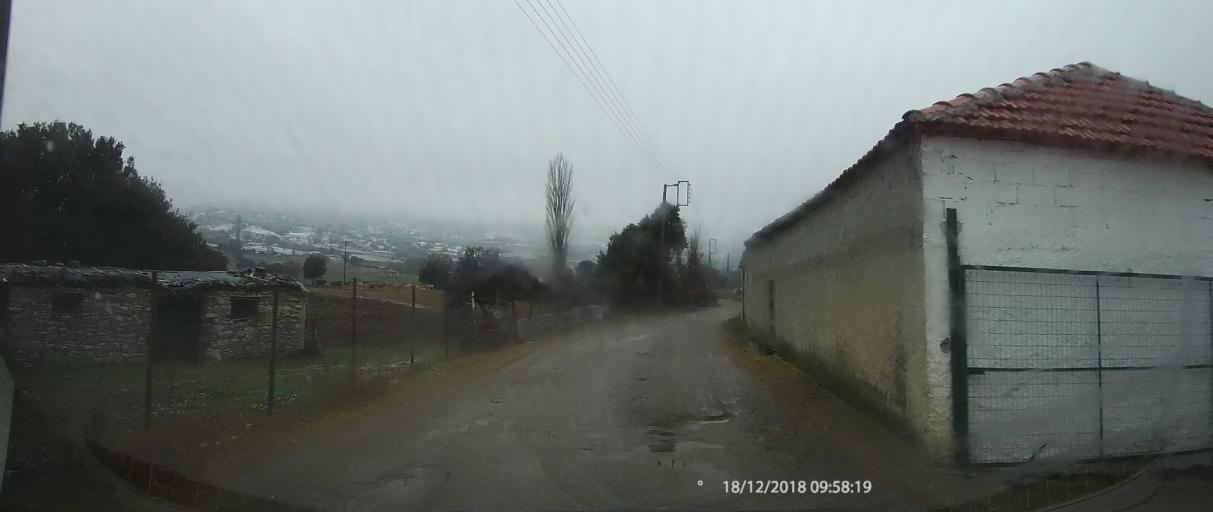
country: GR
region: Thessaly
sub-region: Nomos Larisis
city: Livadi
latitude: 40.0265
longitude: 22.2413
